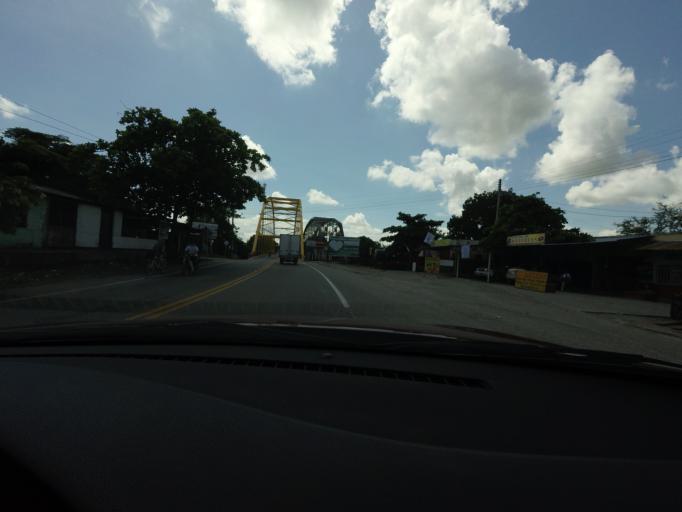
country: CO
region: Tolima
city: Saldana
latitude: 3.9357
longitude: -75.0192
